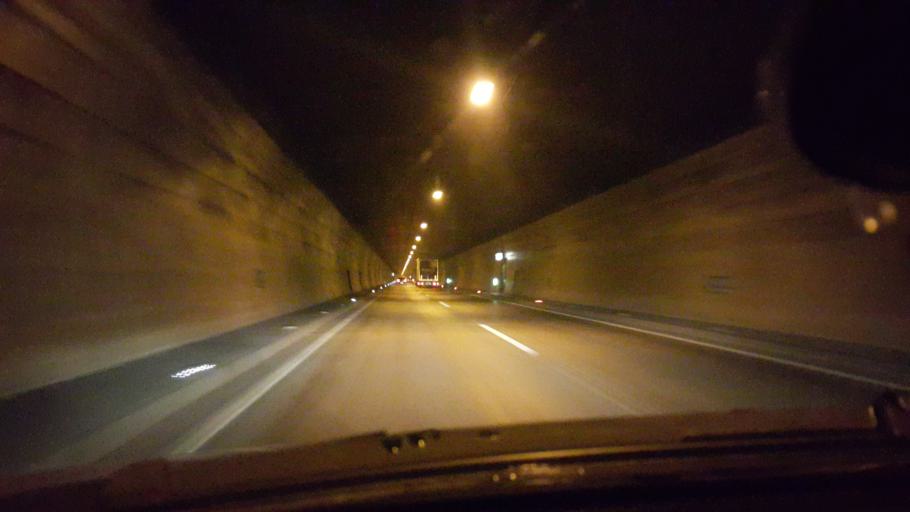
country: AT
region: Styria
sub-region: Graz Stadt
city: Goesting
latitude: 47.0999
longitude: 15.3818
